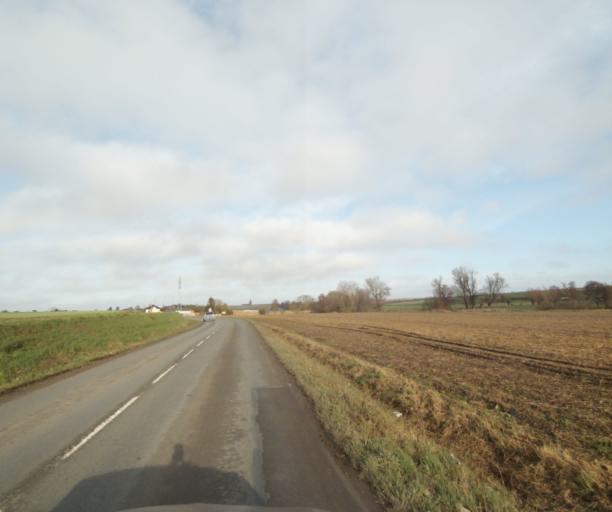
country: FR
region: Nord-Pas-de-Calais
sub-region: Departement du Nord
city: Thiant
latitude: 50.2916
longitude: 3.4484
